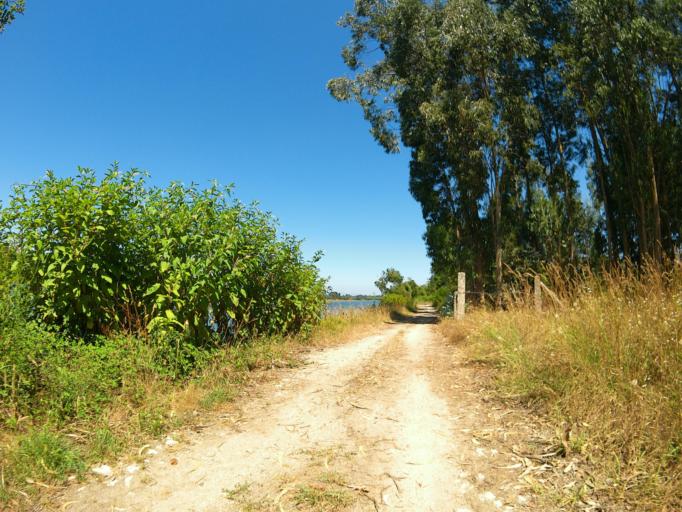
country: PT
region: Viana do Castelo
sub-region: Viana do Castelo
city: Darque
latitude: 41.6960
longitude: -8.7590
